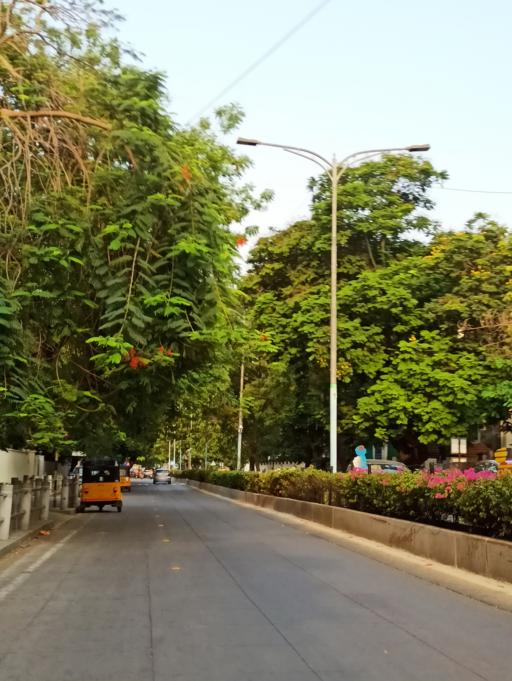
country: IN
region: Tamil Nadu
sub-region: Chennai
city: Chetput
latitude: 13.0694
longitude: 80.2384
